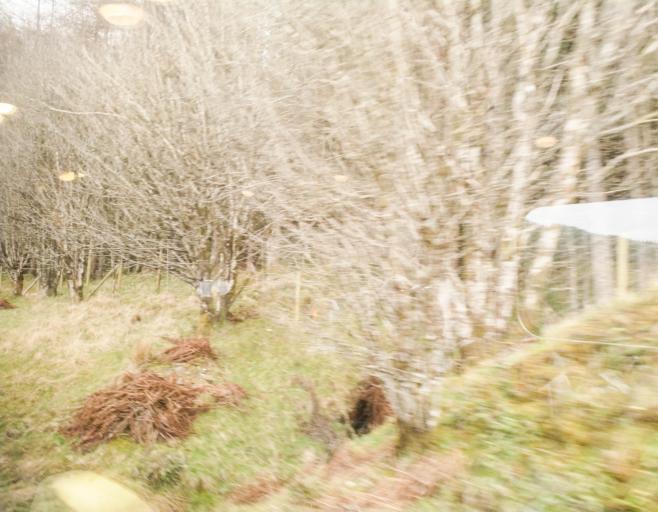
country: GB
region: Scotland
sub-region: Argyll and Bute
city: Garelochhead
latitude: 56.4429
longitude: -4.7079
